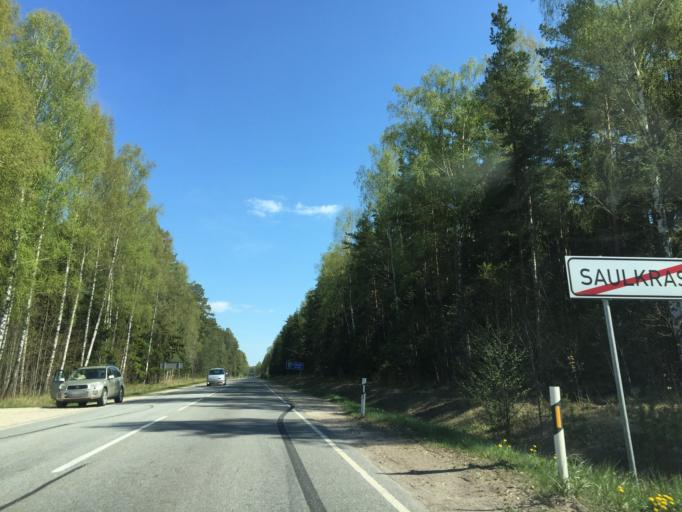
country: LV
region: Saulkrastu
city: Saulkrasti
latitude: 57.3225
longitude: 24.4271
